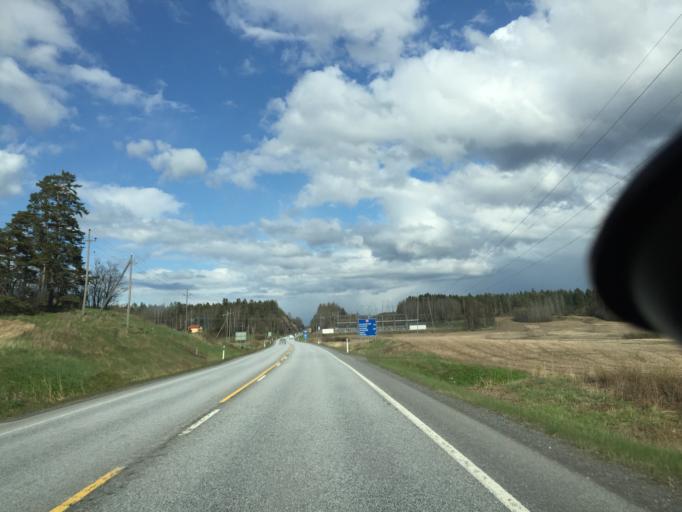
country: FI
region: Uusimaa
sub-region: Raaseporin
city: Karis
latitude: 60.0453
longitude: 23.6308
